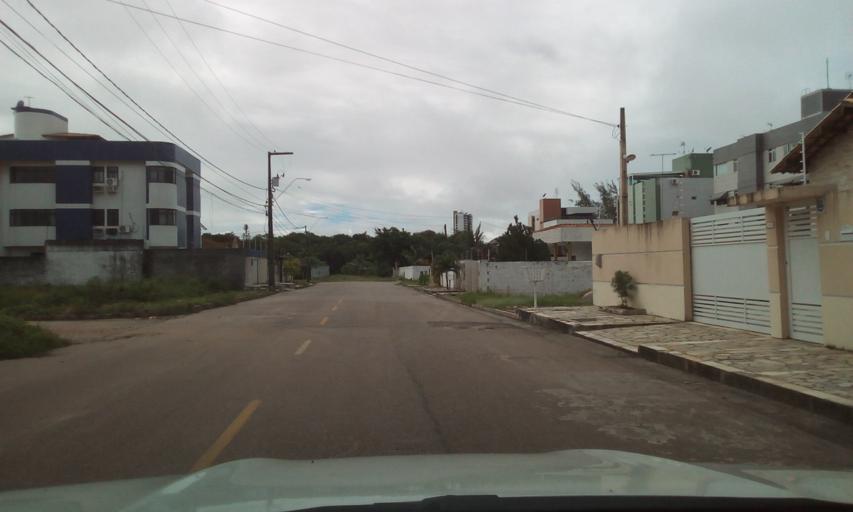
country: BR
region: Paraiba
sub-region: Joao Pessoa
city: Joao Pessoa
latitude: -7.0604
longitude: -34.8465
